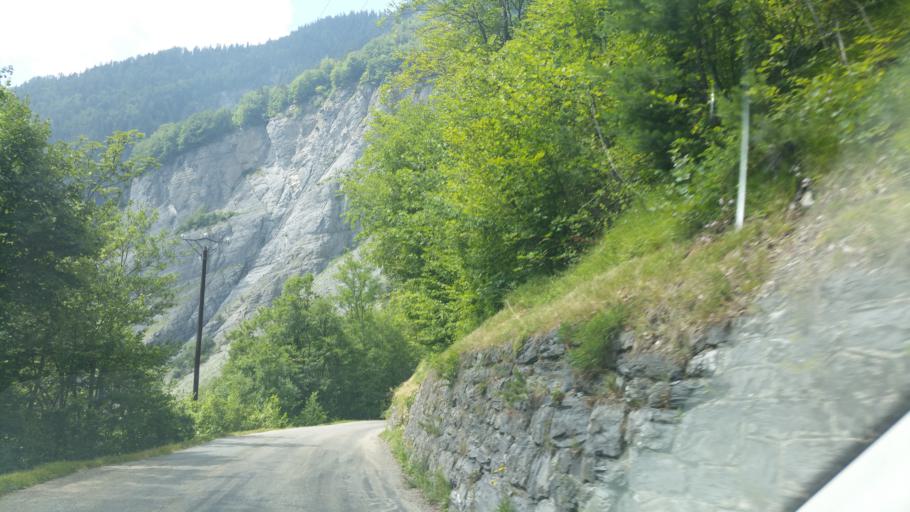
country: FR
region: Rhone-Alpes
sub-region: Departement de la Savoie
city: Saint-Jean-de-Maurienne
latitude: 45.2254
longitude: 6.3094
